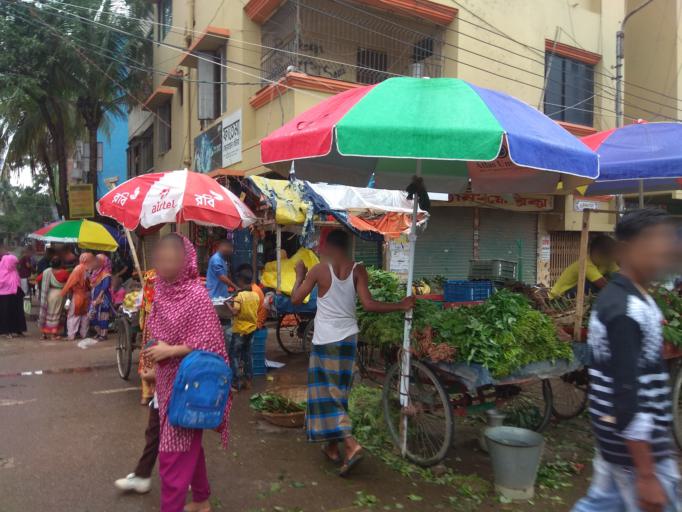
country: BD
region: Dhaka
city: Tungi
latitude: 23.8196
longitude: 90.3714
